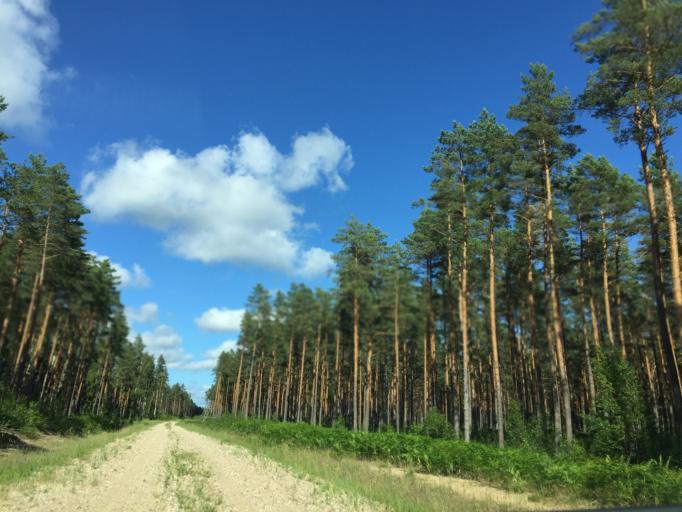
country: LV
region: Ventspils
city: Ventspils
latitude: 57.5316
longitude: 21.7198
